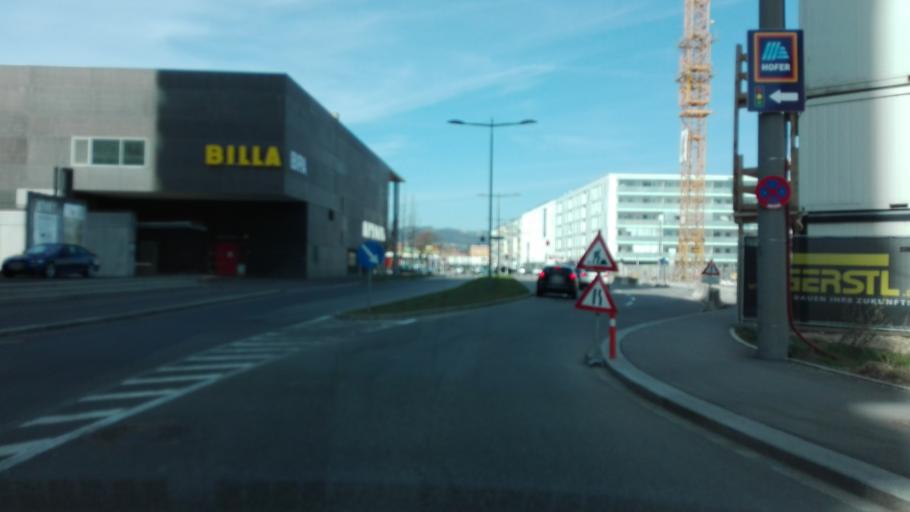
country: AT
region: Upper Austria
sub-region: Linz Stadt
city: Linz
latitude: 48.2914
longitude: 14.3054
